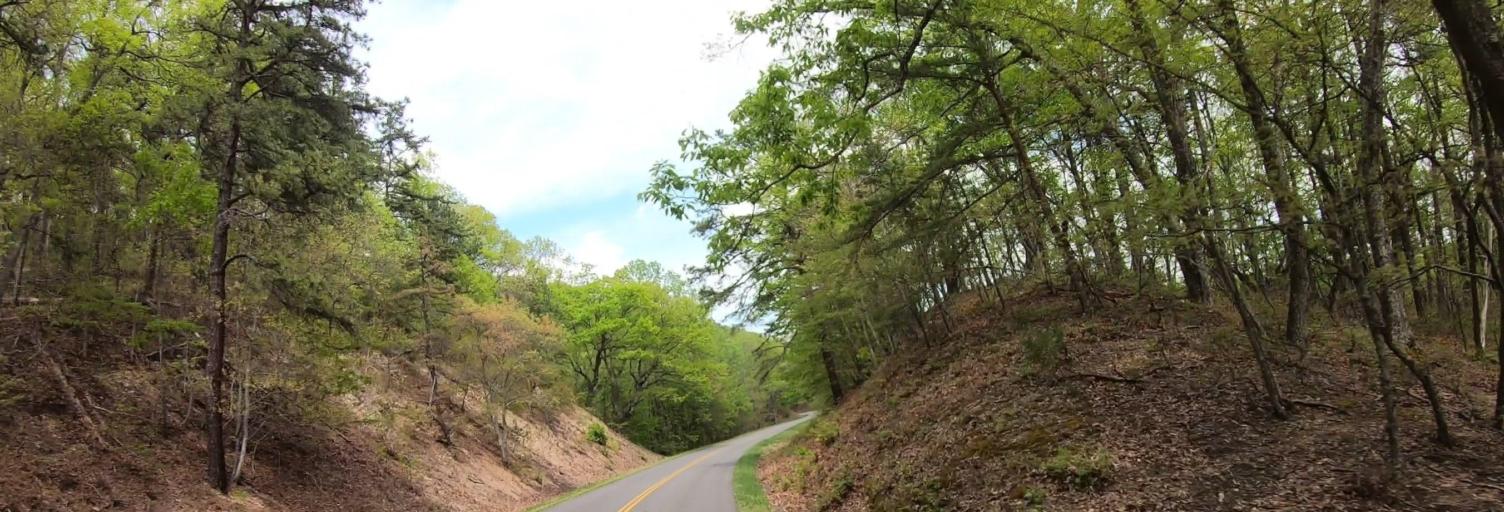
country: US
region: Virginia
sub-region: Botetourt County
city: Blue Ridge
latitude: 37.4026
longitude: -79.8295
